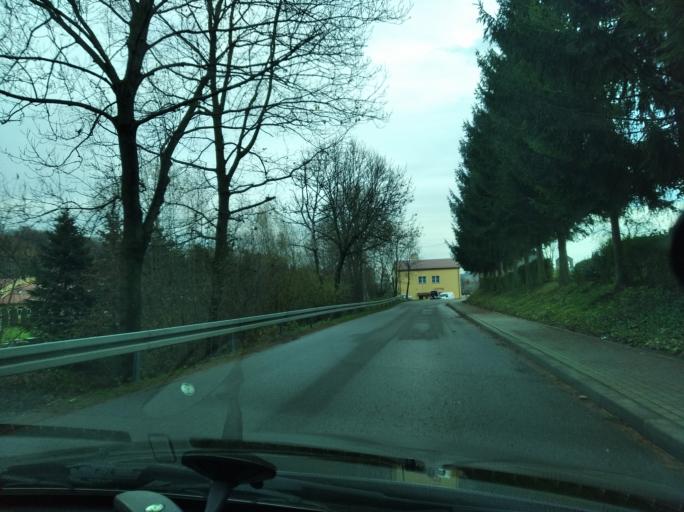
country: PL
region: Subcarpathian Voivodeship
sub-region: Powiat strzyzowski
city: Strzyzow
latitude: 49.9352
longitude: 21.7609
